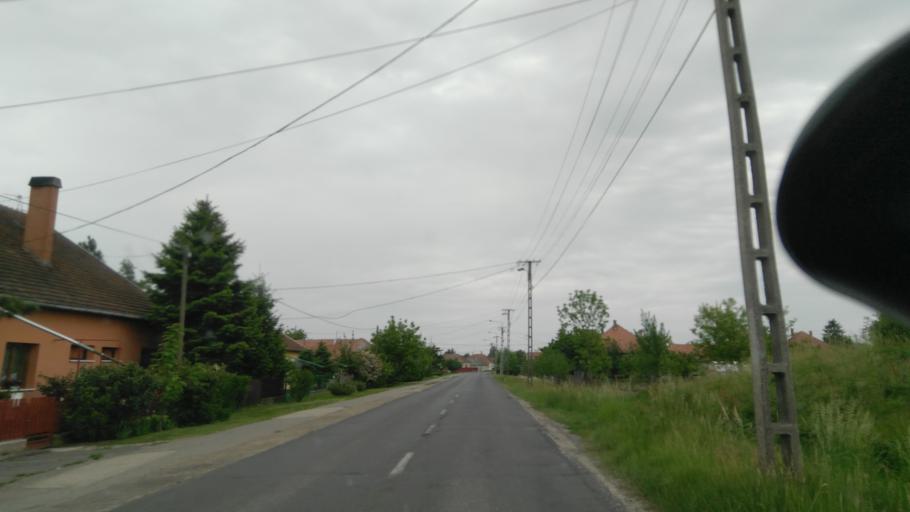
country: HU
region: Bekes
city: Doboz
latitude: 46.7336
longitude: 21.2564
